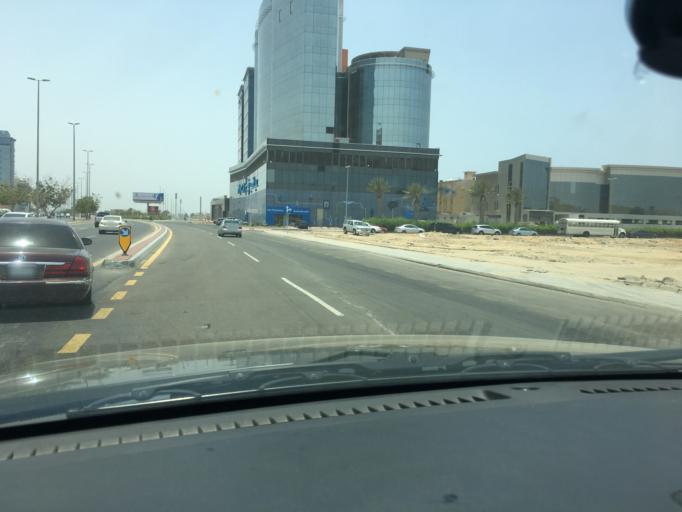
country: SA
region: Makkah
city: Jeddah
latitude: 21.6604
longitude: 39.1225
